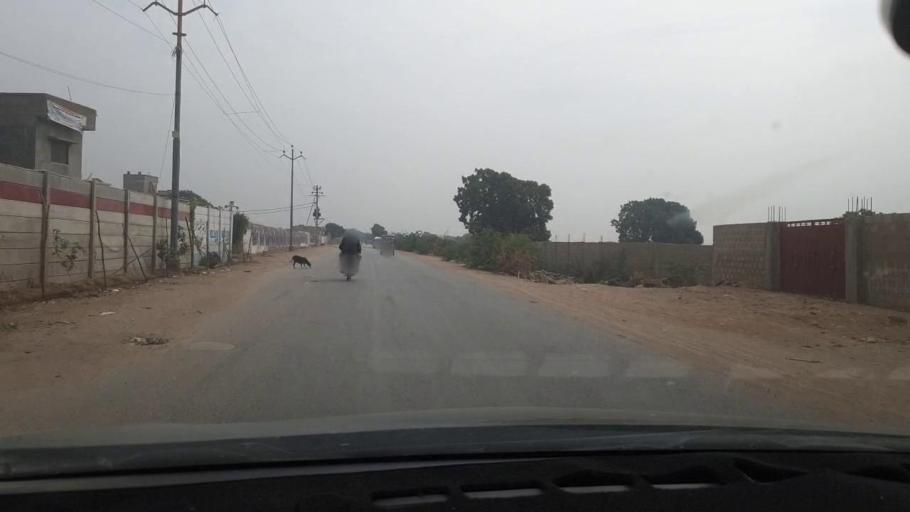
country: PK
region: Sindh
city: Malir Cantonment
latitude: 24.9179
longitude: 67.2590
